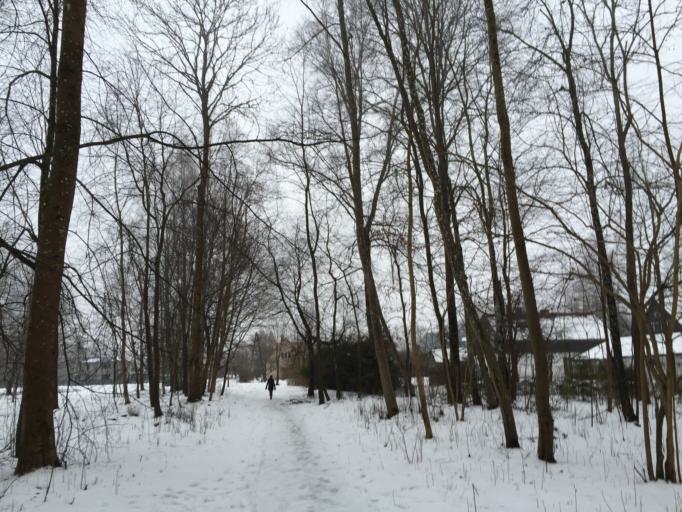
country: LV
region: Sigulda
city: Sigulda
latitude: 57.1699
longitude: 24.8646
